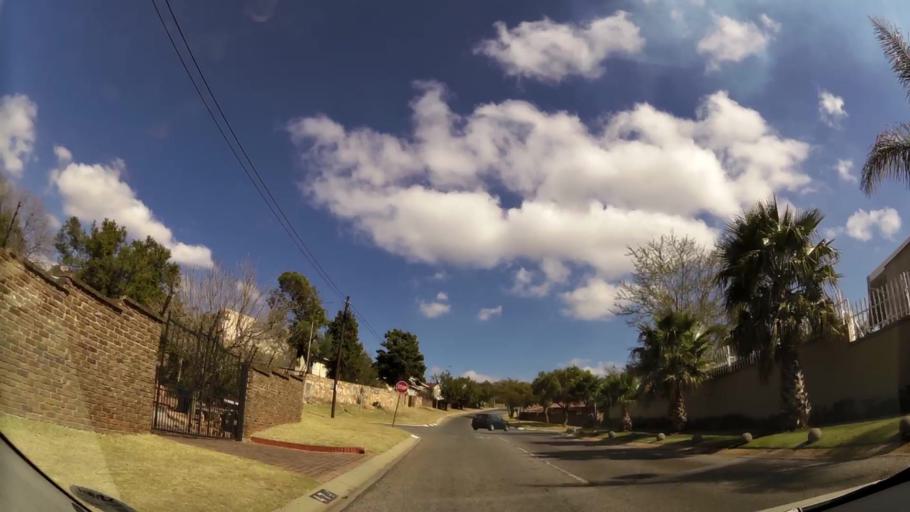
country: ZA
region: Gauteng
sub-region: City of Johannesburg Metropolitan Municipality
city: Roodepoort
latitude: -26.1171
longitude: 27.8412
